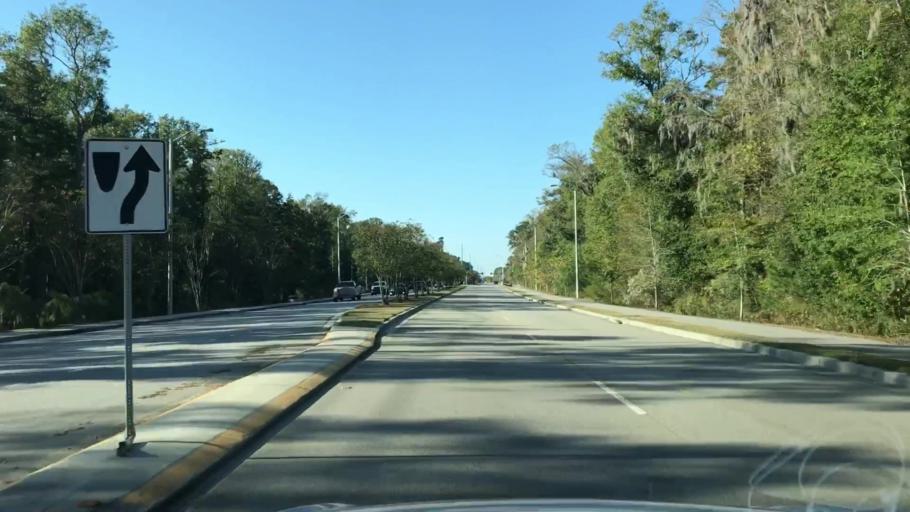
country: US
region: South Carolina
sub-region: Charleston County
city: Shell Point
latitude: 32.8113
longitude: -80.1070
